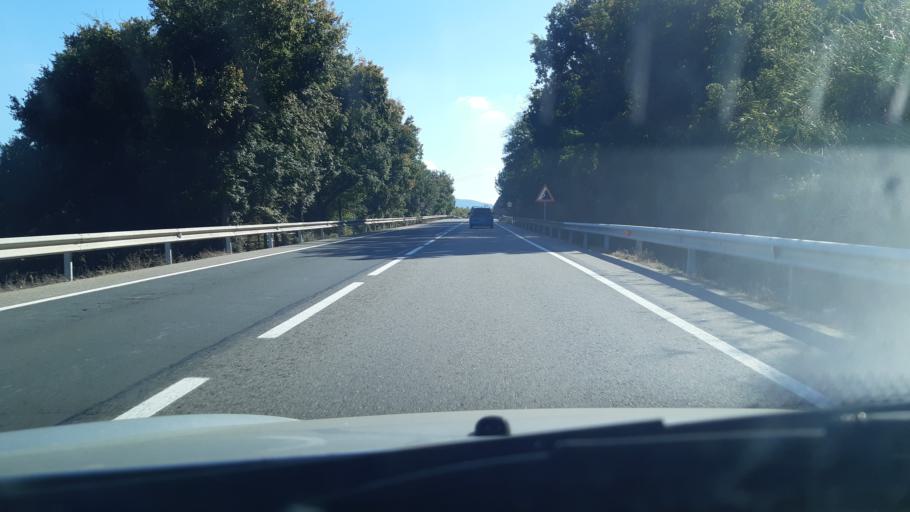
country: ES
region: Catalonia
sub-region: Provincia de Tarragona
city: Tivenys
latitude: 40.8636
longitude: 0.5069
